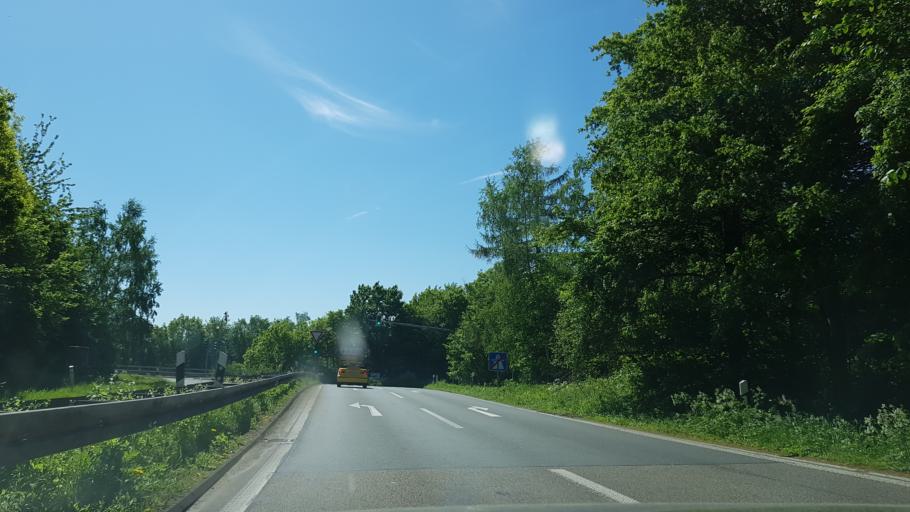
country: DE
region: North Rhine-Westphalia
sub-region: Regierungsbezirk Dusseldorf
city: Ratingen
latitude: 51.2963
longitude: 6.8866
